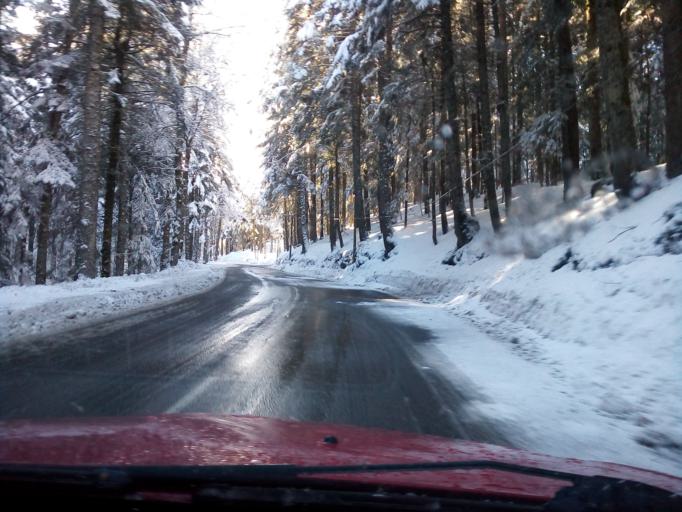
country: FR
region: Rhone-Alpes
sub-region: Departement de l'Isere
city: Le Sappey-en-Chartreuse
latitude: 45.3015
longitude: 5.7709
